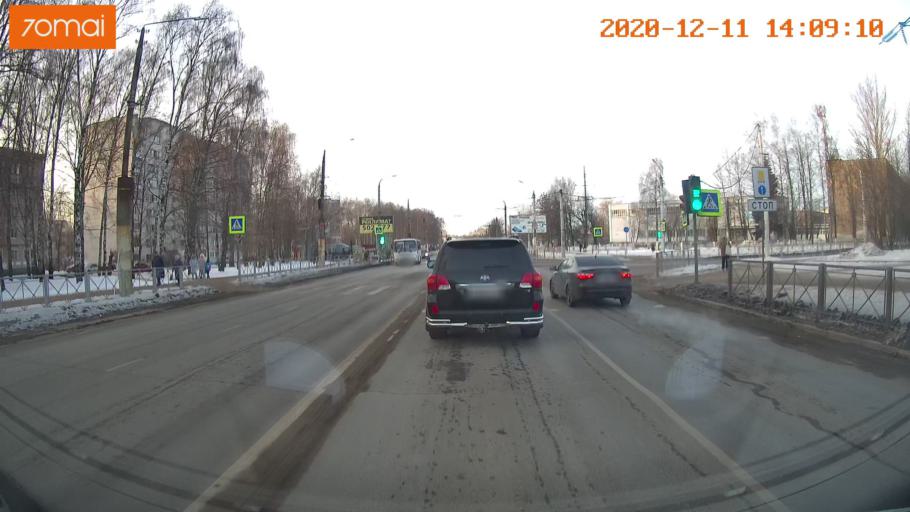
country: RU
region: Kostroma
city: Oktyabr'skiy
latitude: 57.7385
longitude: 40.9895
